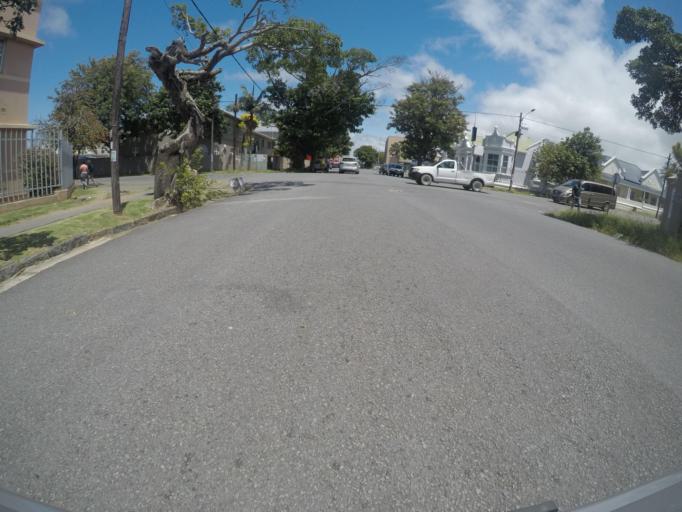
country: ZA
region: Eastern Cape
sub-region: Buffalo City Metropolitan Municipality
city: East London
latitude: -32.9994
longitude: 27.8994
